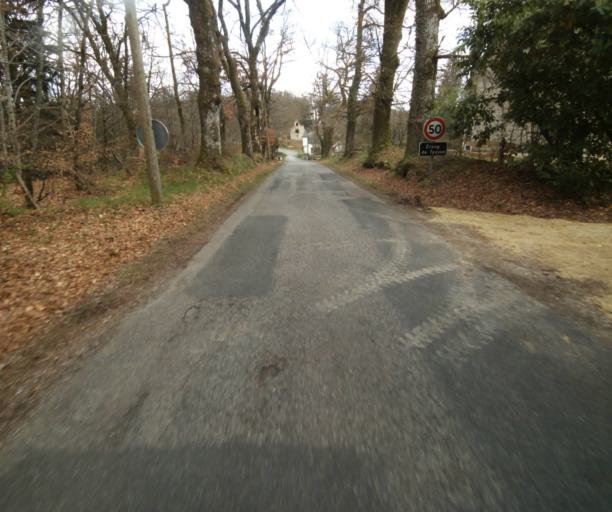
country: FR
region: Limousin
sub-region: Departement de la Correze
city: Correze
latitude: 45.2590
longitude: 1.9119
